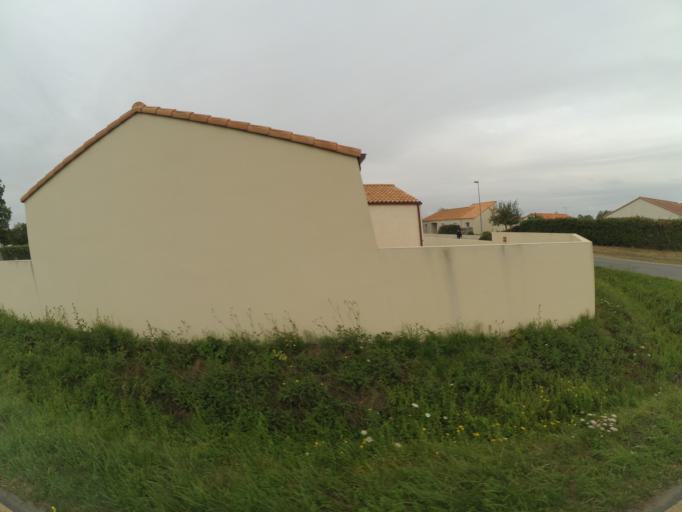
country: FR
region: Pays de la Loire
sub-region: Departement de la Vendee
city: Saint-Andre-Treize-Voies
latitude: 46.9376
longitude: -1.4075
